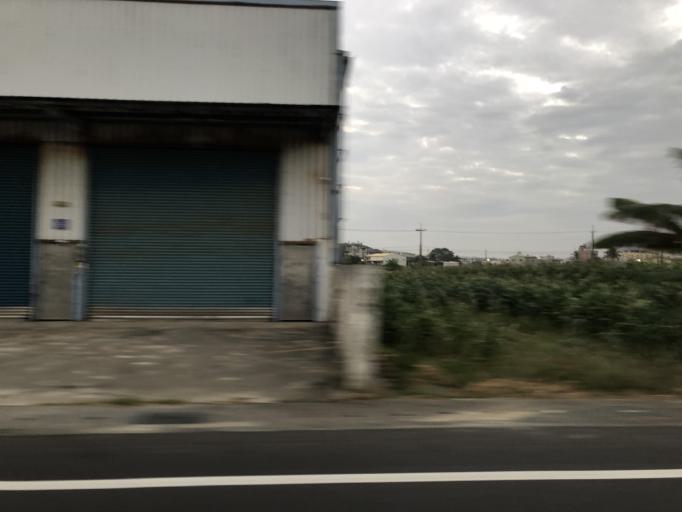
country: TW
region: Taiwan
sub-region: Tainan
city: Tainan
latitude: 23.0210
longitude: 120.2732
